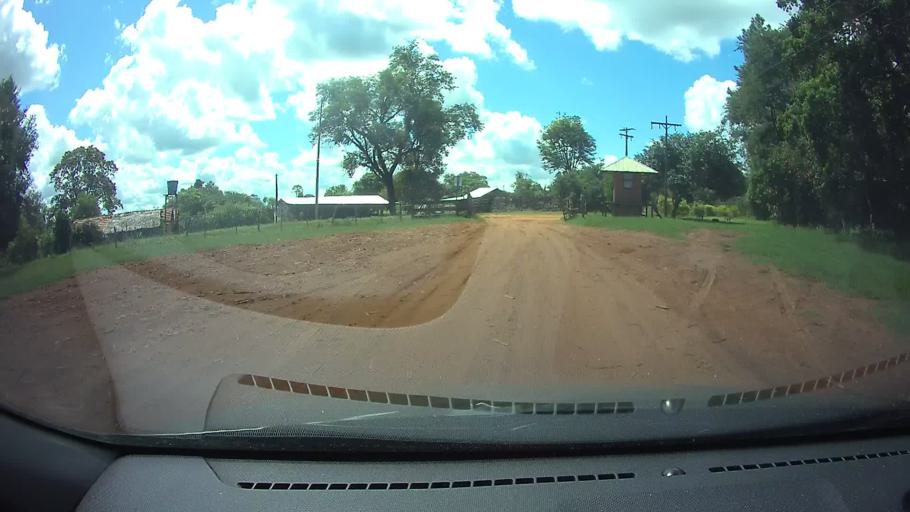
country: PY
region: Paraguari
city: La Colmena
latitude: -25.9508
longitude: -56.7826
